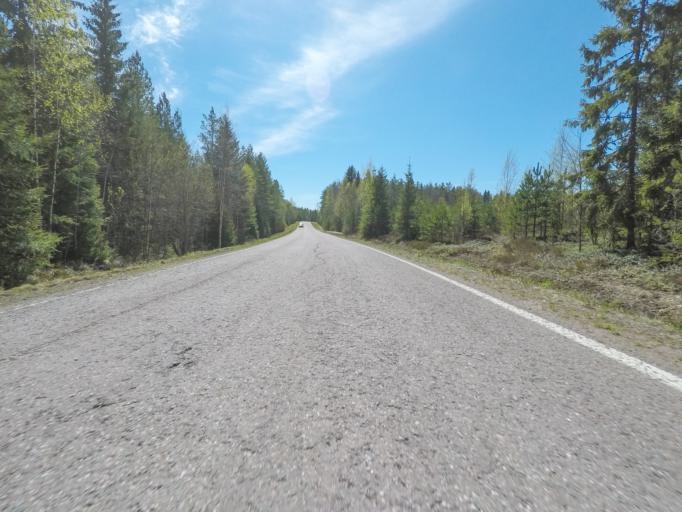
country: FI
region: Uusimaa
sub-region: Helsinki
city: Kaerkoelae
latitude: 60.5954
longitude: 23.8011
